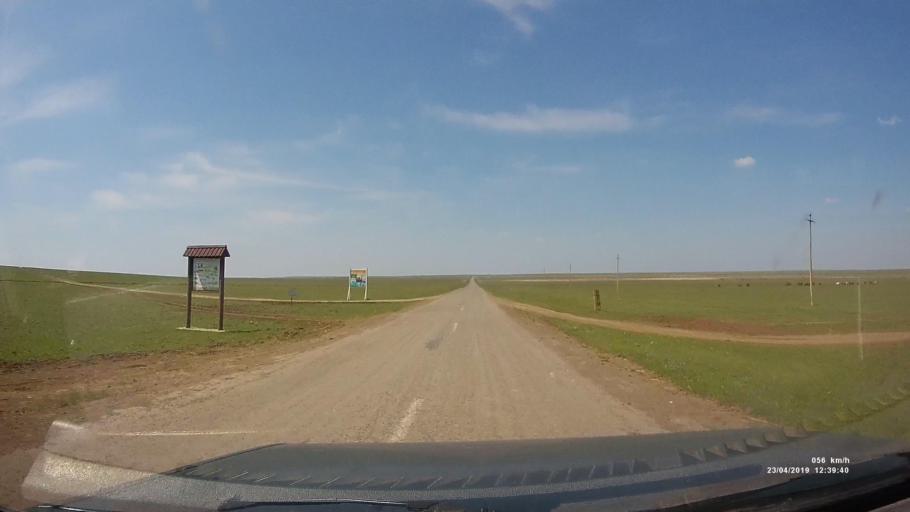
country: RU
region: Kalmykiya
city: Yashalta
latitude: 46.4355
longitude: 42.7062
